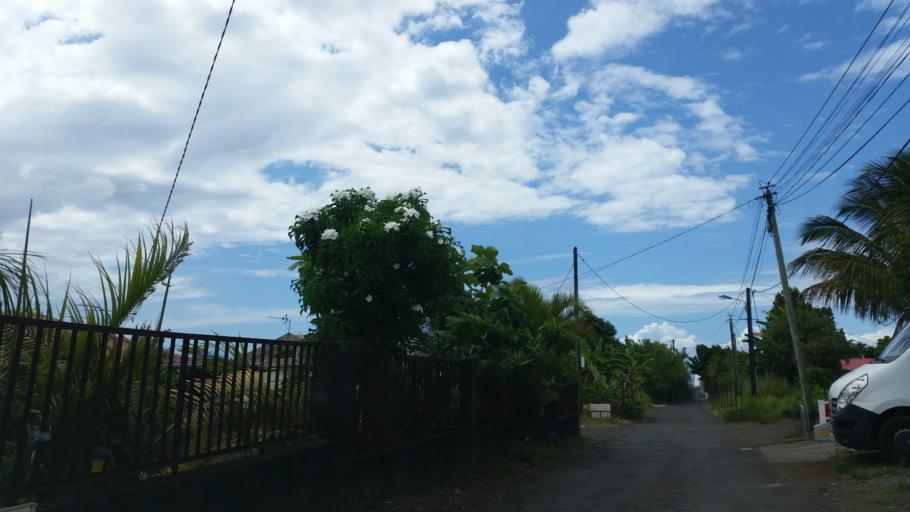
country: RE
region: Reunion
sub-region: Reunion
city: Sainte-Marie
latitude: -20.9293
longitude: 55.5217
